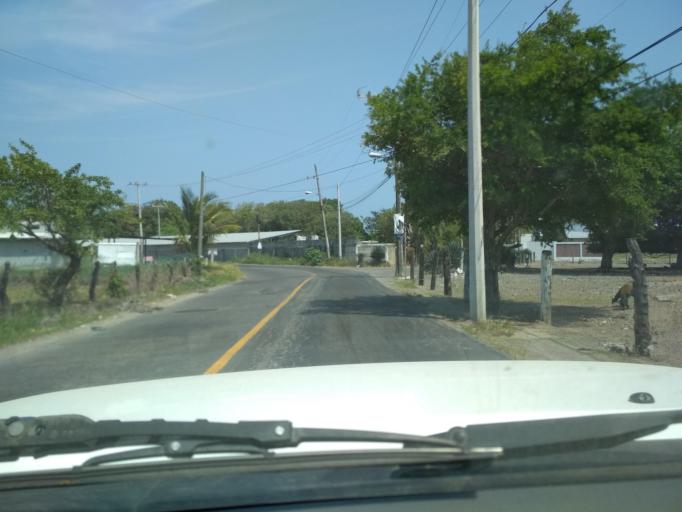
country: MX
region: Veracruz
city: Boca del Rio
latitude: 19.0950
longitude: -96.1182
